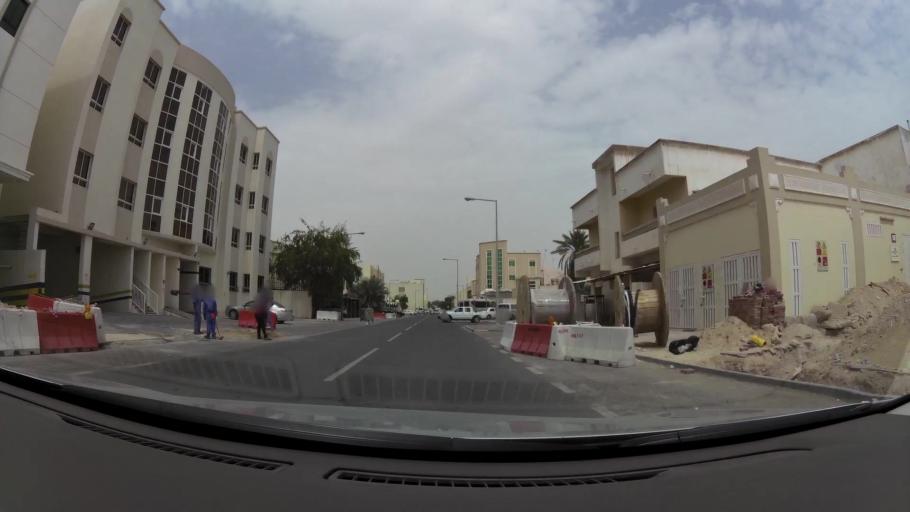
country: QA
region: Baladiyat ar Rayyan
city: Ar Rayyan
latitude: 25.3170
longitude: 51.4746
